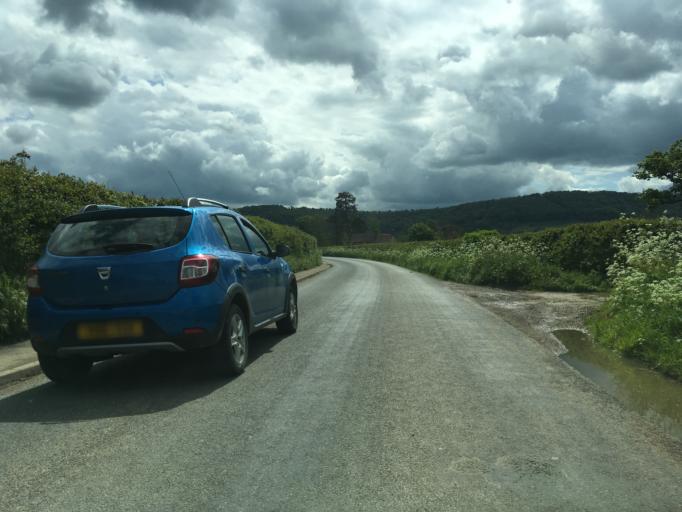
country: GB
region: England
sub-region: Gloucestershire
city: Stonehouse
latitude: 51.7338
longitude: -2.2857
